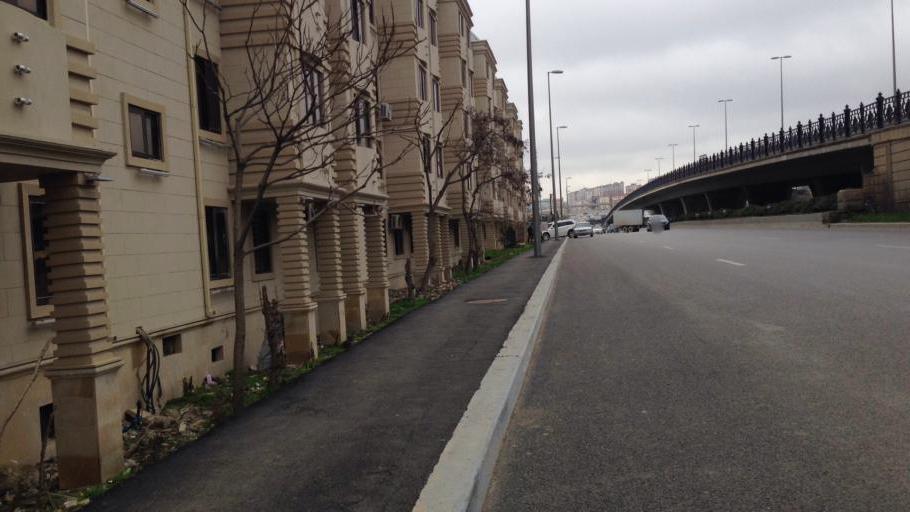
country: AZ
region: Baki
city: Bilajari
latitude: 40.4109
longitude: 49.8370
